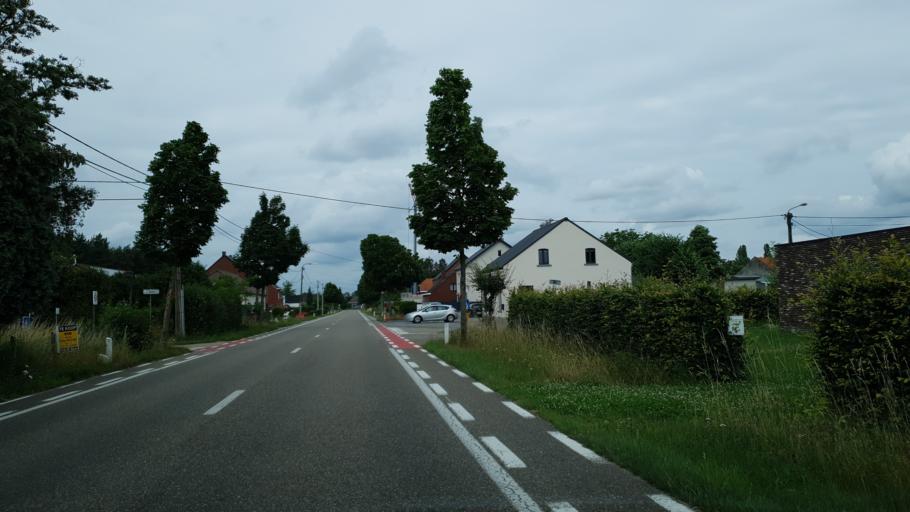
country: BE
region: Flanders
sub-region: Provincie Antwerpen
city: Laakdal
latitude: 51.0555
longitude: 4.9931
